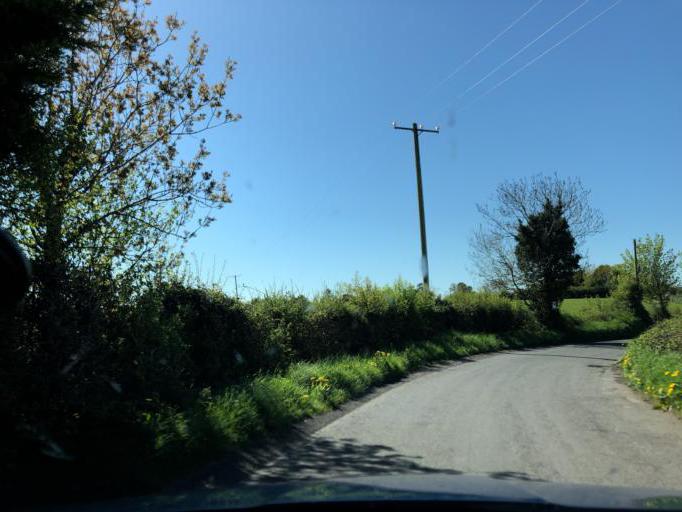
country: IE
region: Connaught
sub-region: County Galway
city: Portumna
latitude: 53.1557
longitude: -8.2945
